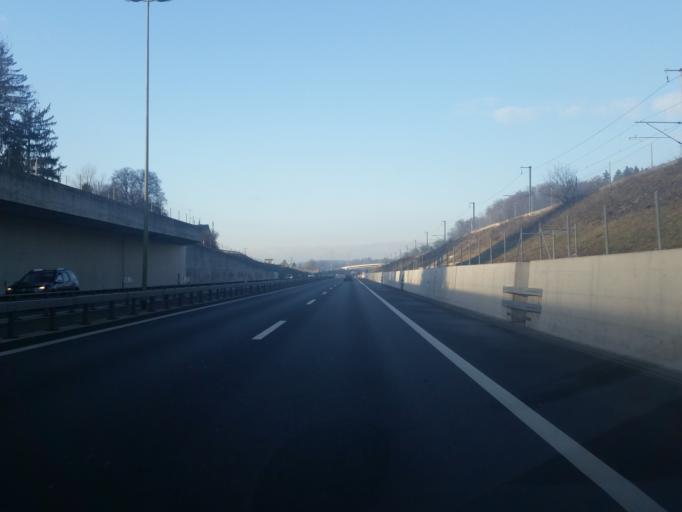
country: CH
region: Zurich
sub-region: Bezirk Affoltern
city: Mettmenstetten
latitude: 47.2524
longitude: 8.4482
